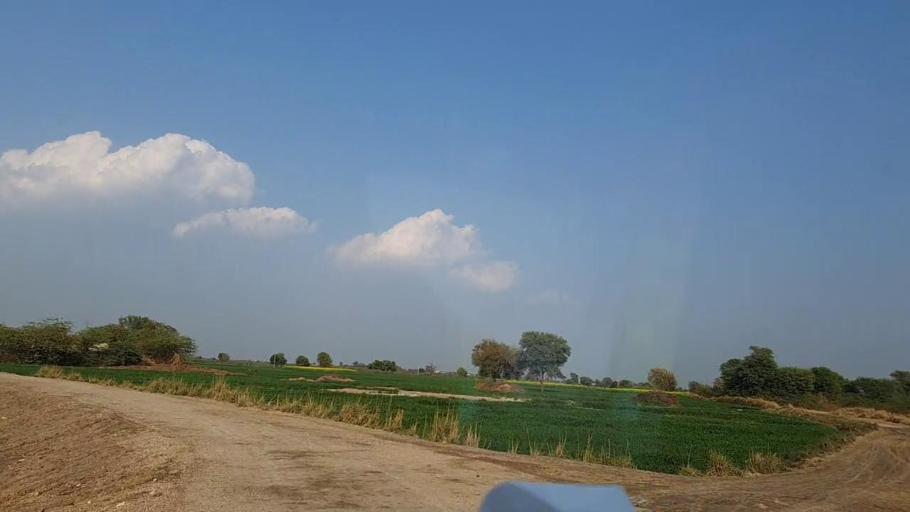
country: PK
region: Sindh
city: Nawabshah
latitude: 26.1603
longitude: 68.4136
